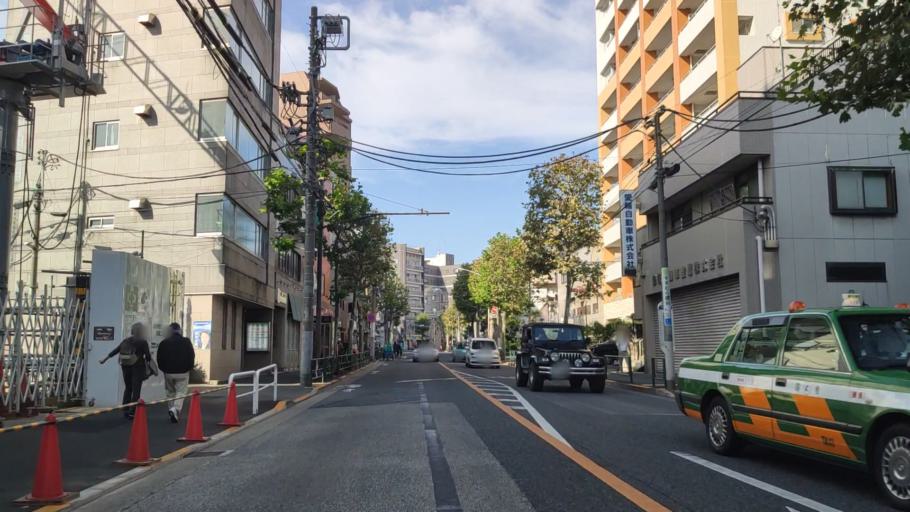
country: JP
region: Tokyo
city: Tokyo
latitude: 35.6945
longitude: 139.6681
